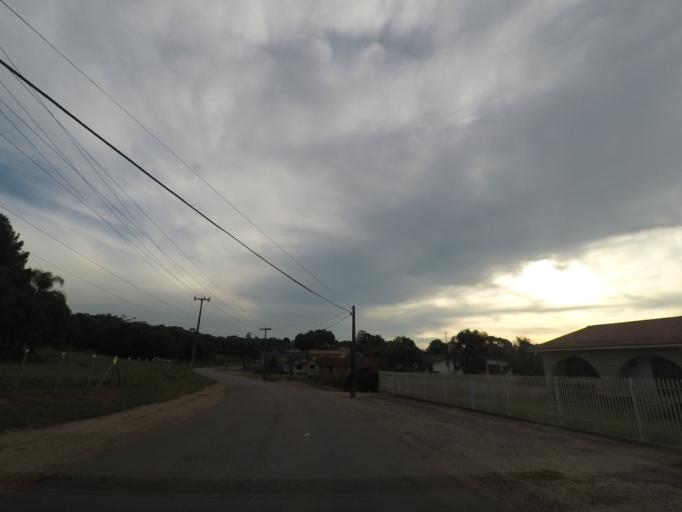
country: BR
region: Parana
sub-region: Colombo
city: Colombo
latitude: -25.2874
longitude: -49.2016
